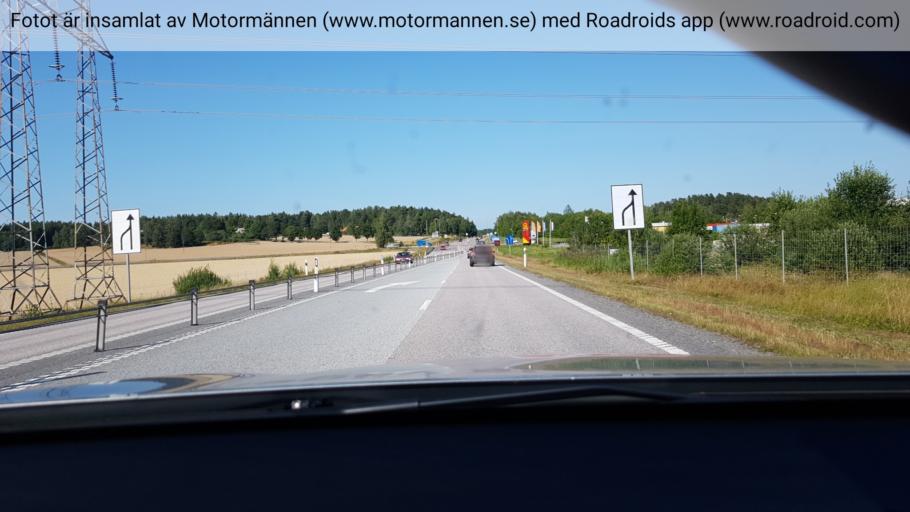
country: SE
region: Uppsala
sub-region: Enkopings Kommun
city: Orsundsbro
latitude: 59.7239
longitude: 17.2876
